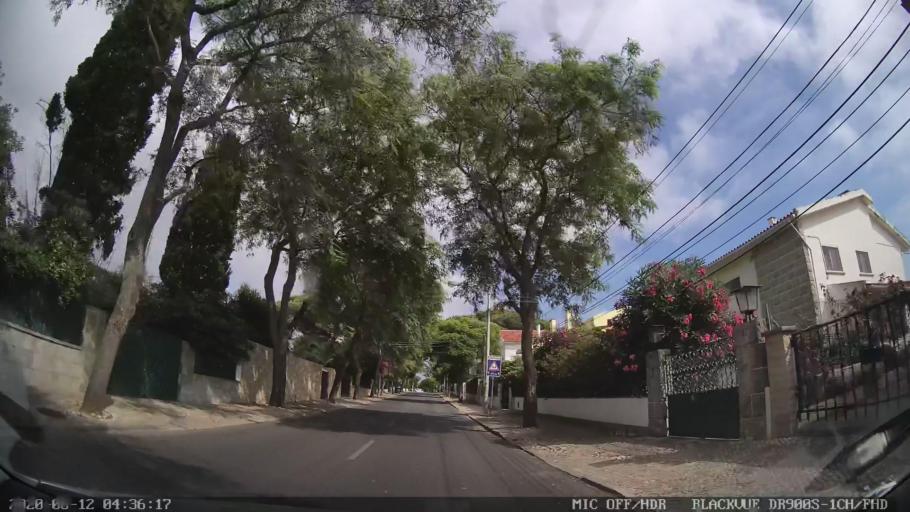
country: PT
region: Lisbon
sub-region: Cascais
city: Estoril
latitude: 38.6980
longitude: -9.3773
